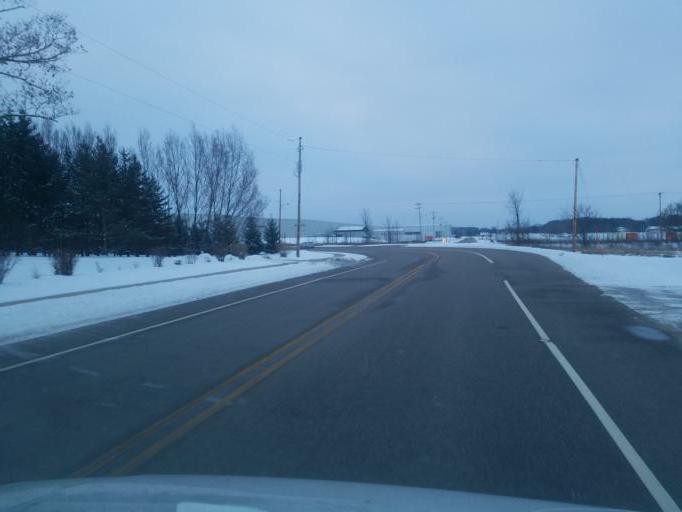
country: US
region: Wisconsin
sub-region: Waupaca County
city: Manawa
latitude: 44.4548
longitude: -88.9201
